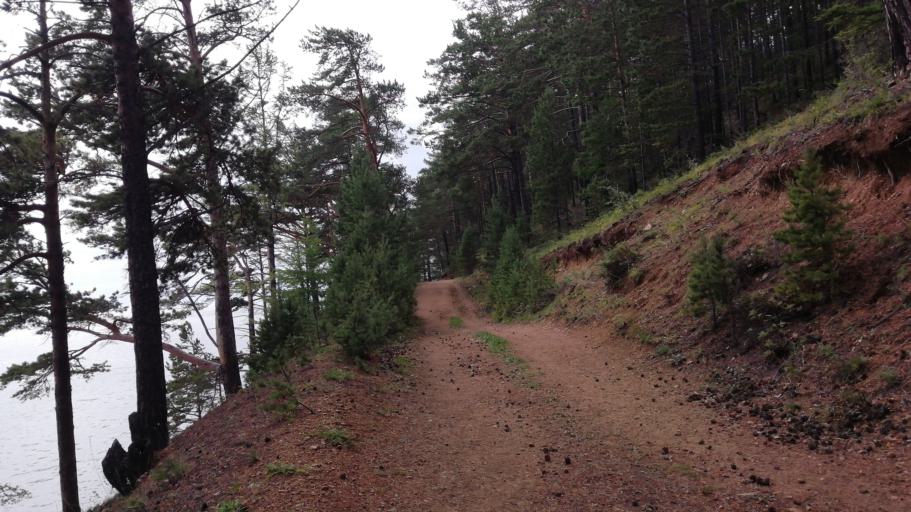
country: RU
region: Irkutsk
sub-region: Irkutskiy Rayon
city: Listvyanka
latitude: 51.8931
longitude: 105.0474
